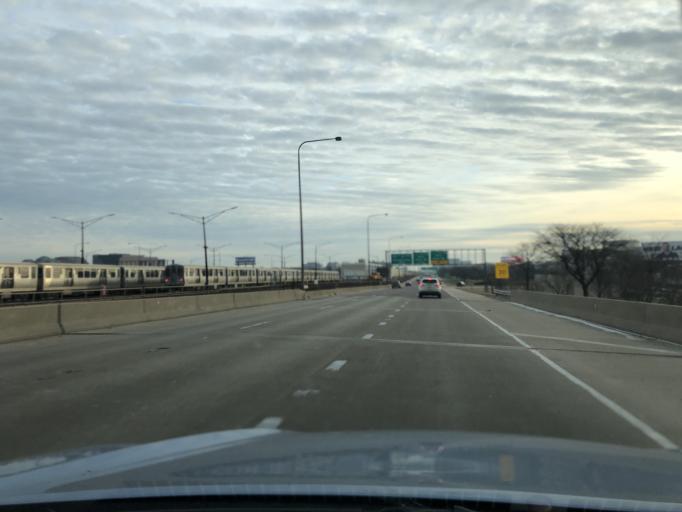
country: US
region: Illinois
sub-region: Cook County
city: Rosemont
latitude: 41.9831
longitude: -87.8678
